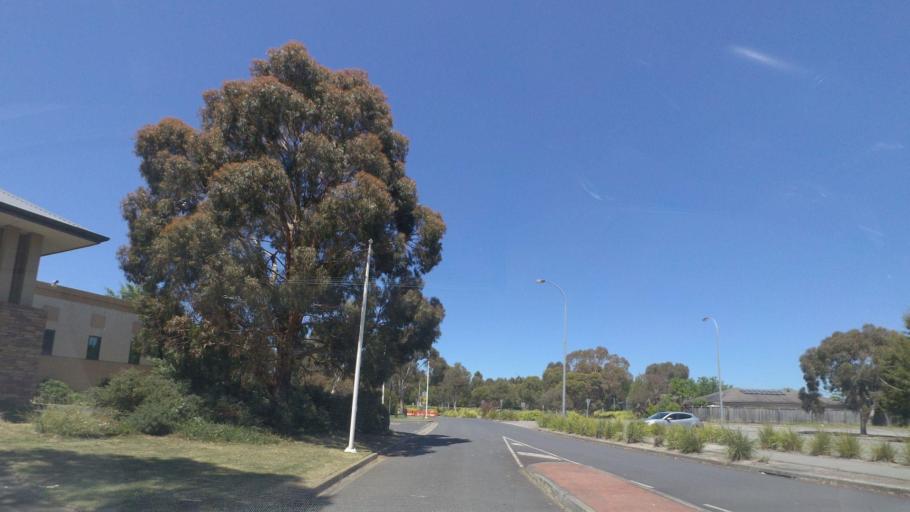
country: AU
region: Victoria
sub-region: Knox
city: Knoxfield
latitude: -37.9021
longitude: 145.2604
